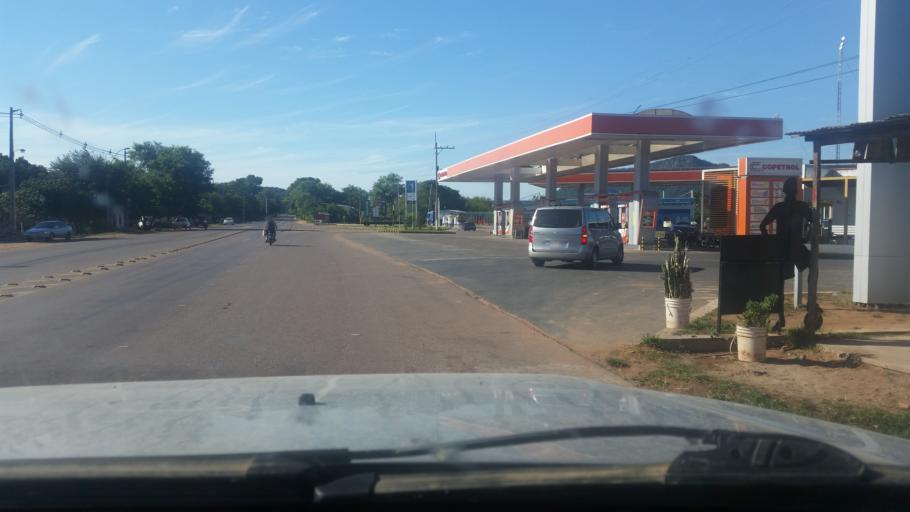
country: PY
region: Paraguari
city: Paraguari
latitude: -25.6317
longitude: -57.1498
